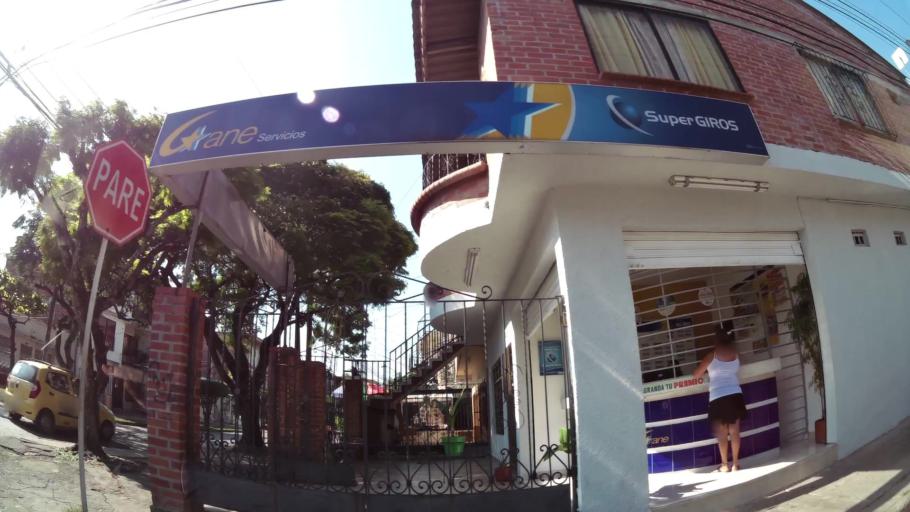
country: CO
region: Valle del Cauca
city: Cali
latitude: 3.4233
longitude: -76.5189
